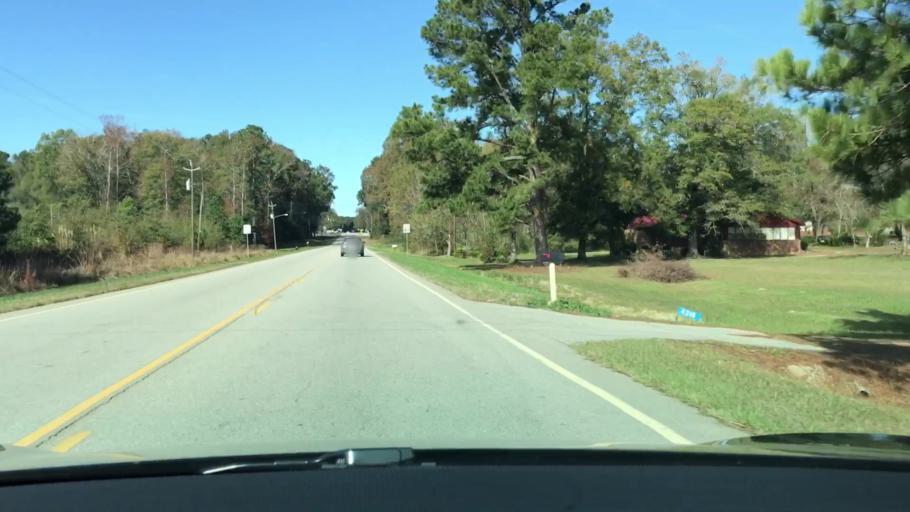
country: US
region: Georgia
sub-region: Warren County
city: Firing Range
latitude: 33.4592
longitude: -82.7020
